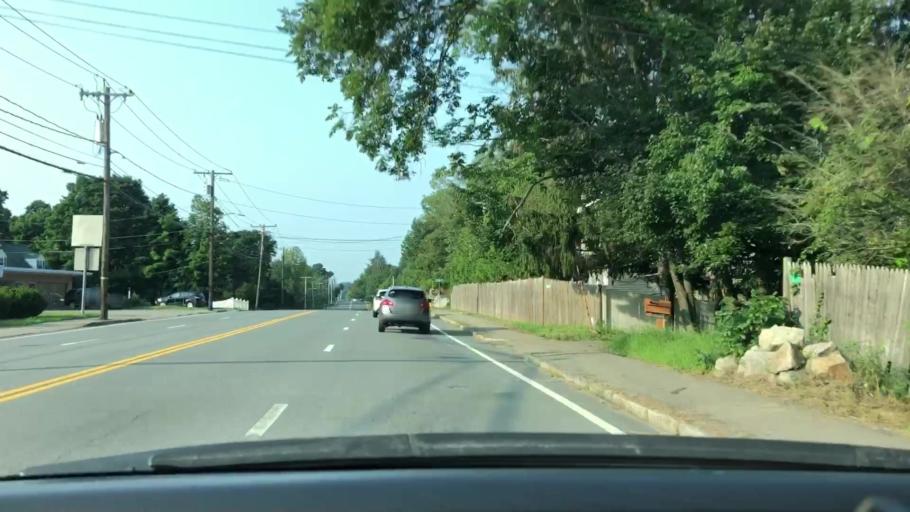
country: US
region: Massachusetts
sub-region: Norfolk County
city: Dedham
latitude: 42.2386
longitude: -71.1812
